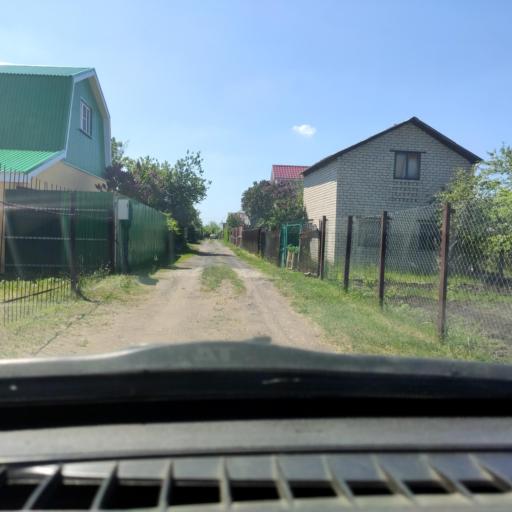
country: RU
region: Samara
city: Povolzhskiy
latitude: 53.5866
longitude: 49.5648
